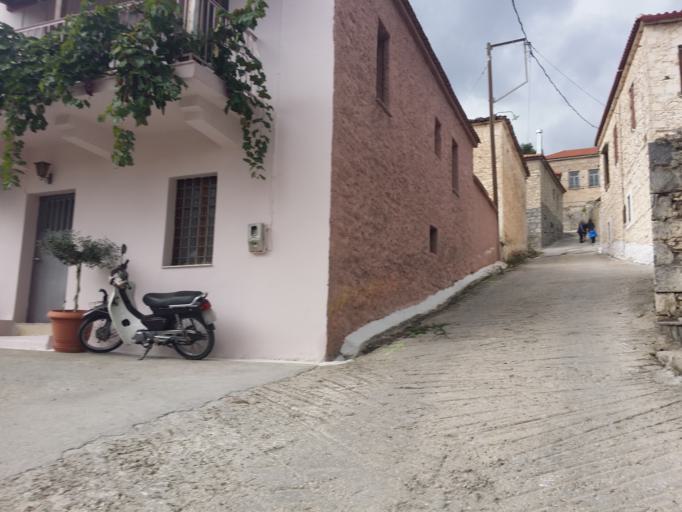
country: GR
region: Peloponnese
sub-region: Nomos Argolidos
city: Koutsopodi
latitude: 37.6398
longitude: 22.5457
